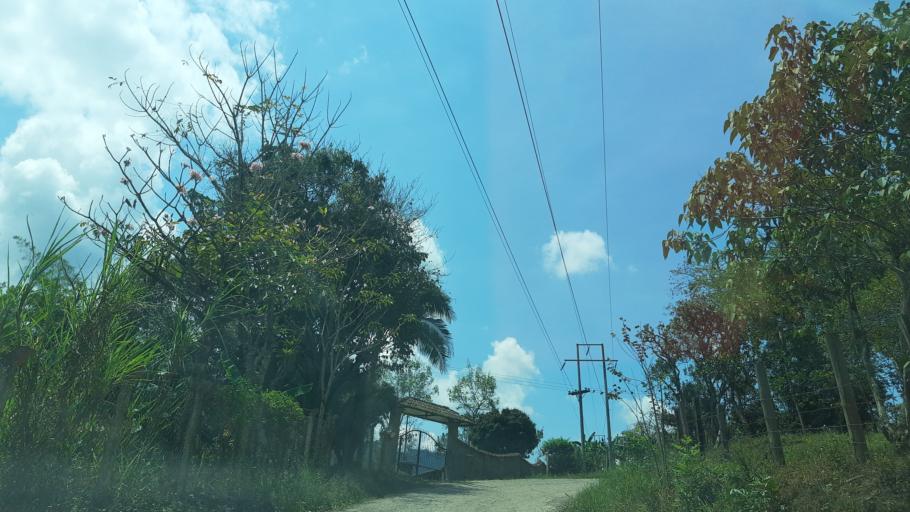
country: CO
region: Boyaca
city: Chinavita
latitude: 5.1319
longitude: -73.3662
